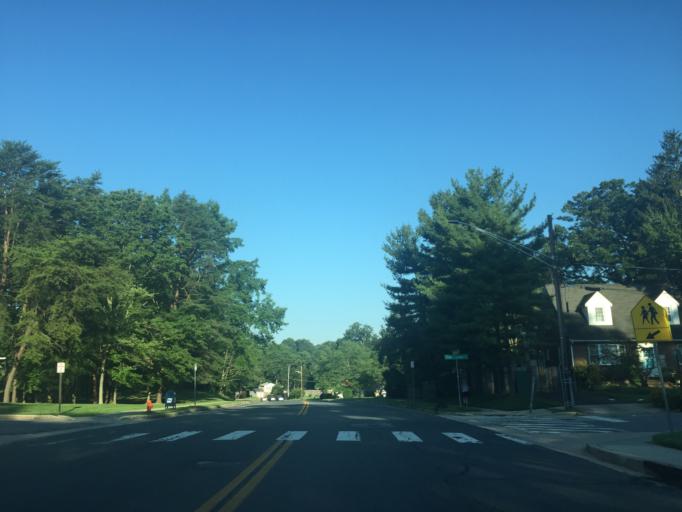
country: US
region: Maryland
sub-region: Howard County
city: Ilchester
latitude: 39.2767
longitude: -76.7699
